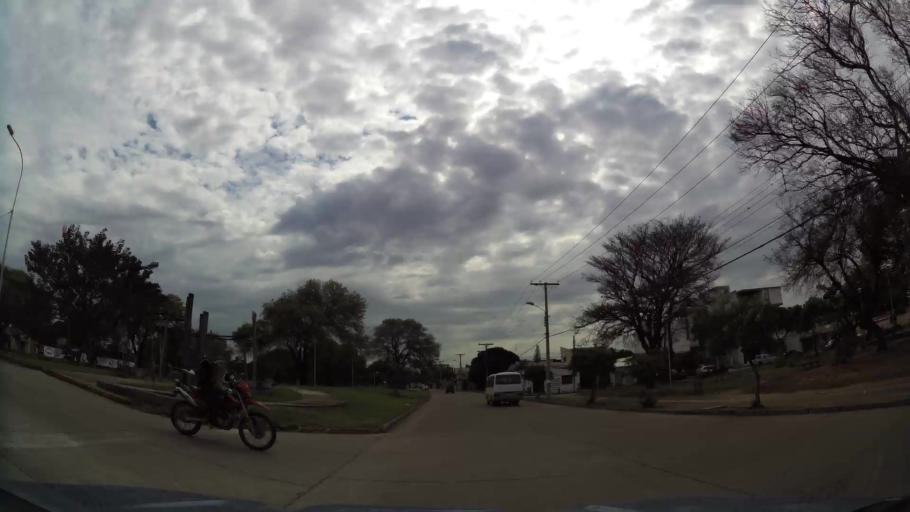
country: BO
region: Santa Cruz
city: Santa Cruz de la Sierra
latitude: -17.7562
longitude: -63.1904
